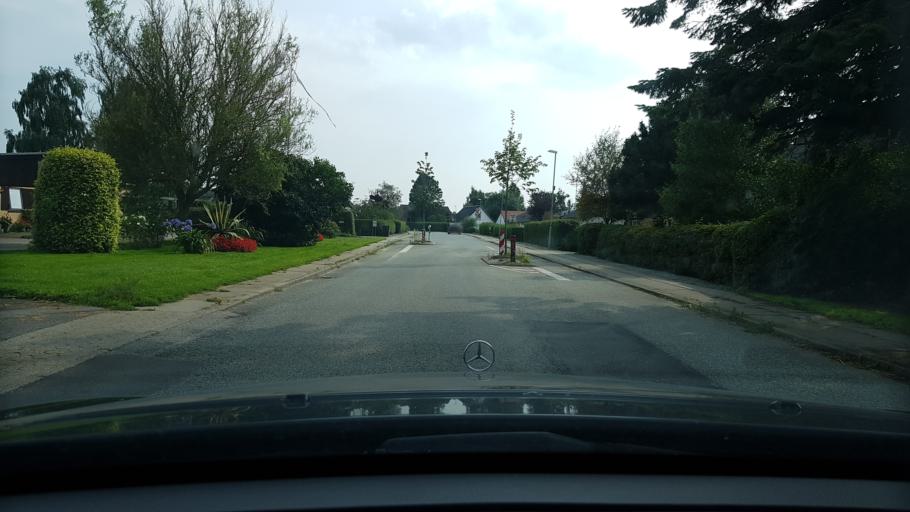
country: DK
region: North Denmark
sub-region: Alborg Kommune
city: Hals
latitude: 56.9717
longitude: 10.2168
